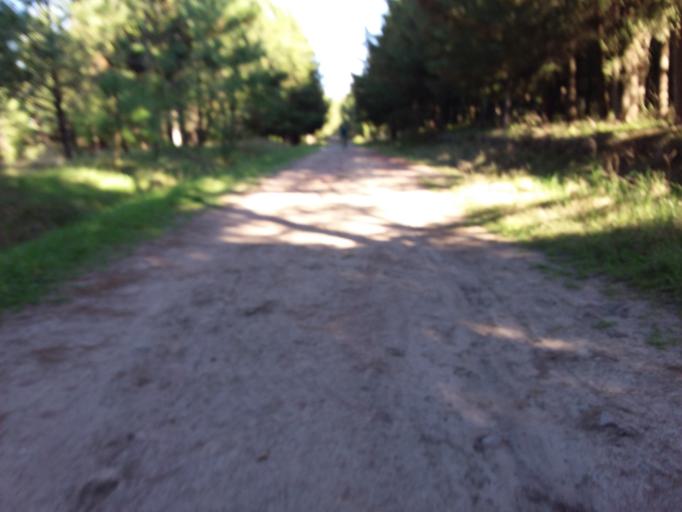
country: MX
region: Mexico
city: San Marcos Yachihuacaltepec
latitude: 19.3127
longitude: -99.6944
